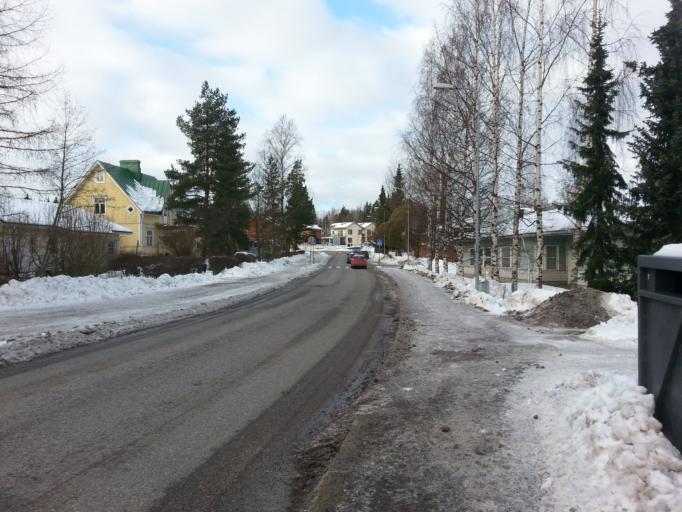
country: FI
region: Uusimaa
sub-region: Helsinki
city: Teekkarikylae
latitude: 60.2369
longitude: 24.8386
